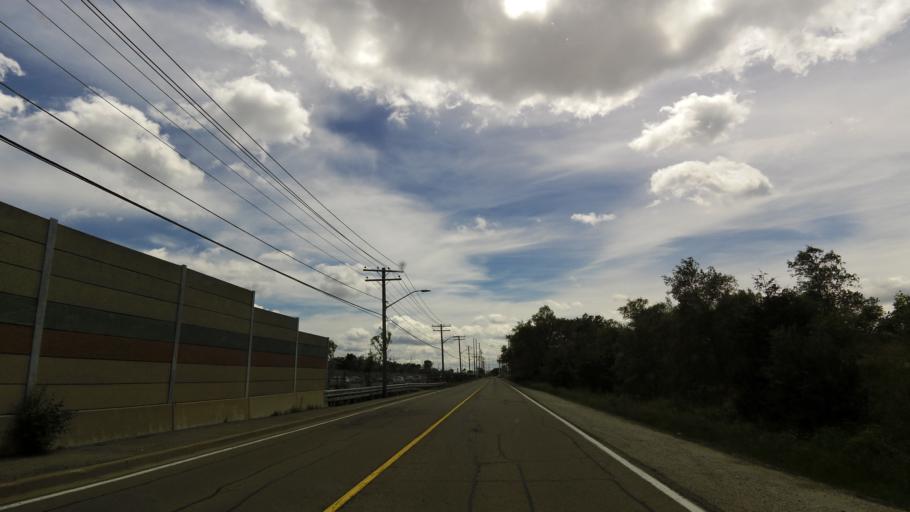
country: CA
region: Ontario
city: Mississauga
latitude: 43.5320
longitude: -79.6399
